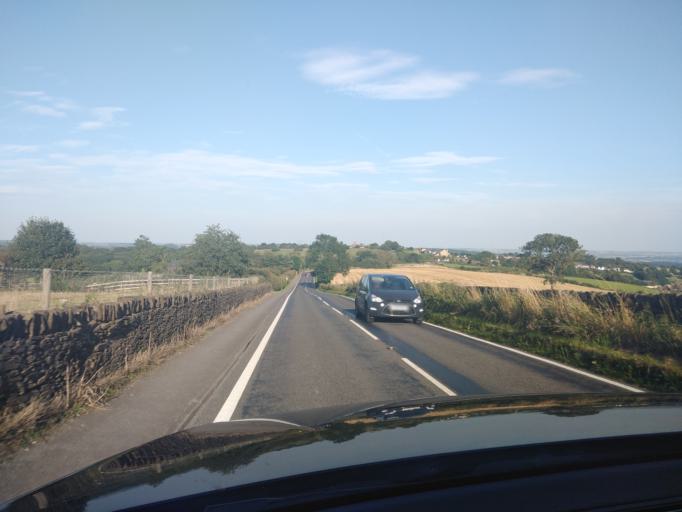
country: GB
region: England
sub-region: Derbyshire
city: Dronfield
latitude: 53.2955
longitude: -1.5338
